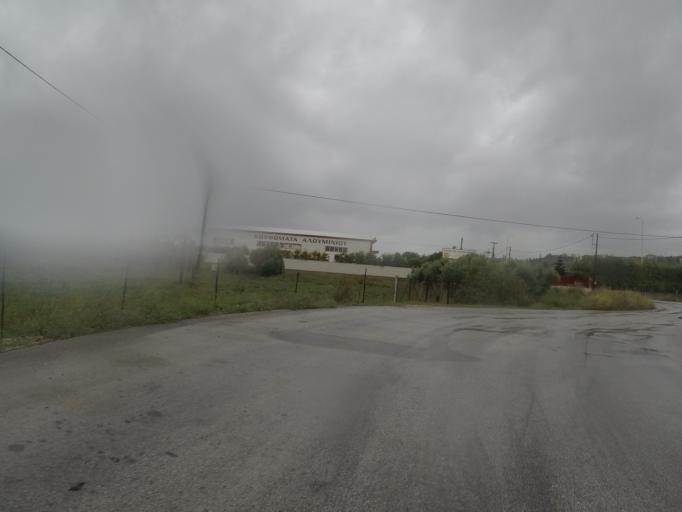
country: GR
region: Peloponnese
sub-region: Nomos Korinthias
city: Arkhaia Korinthos
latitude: 37.9186
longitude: 22.8844
